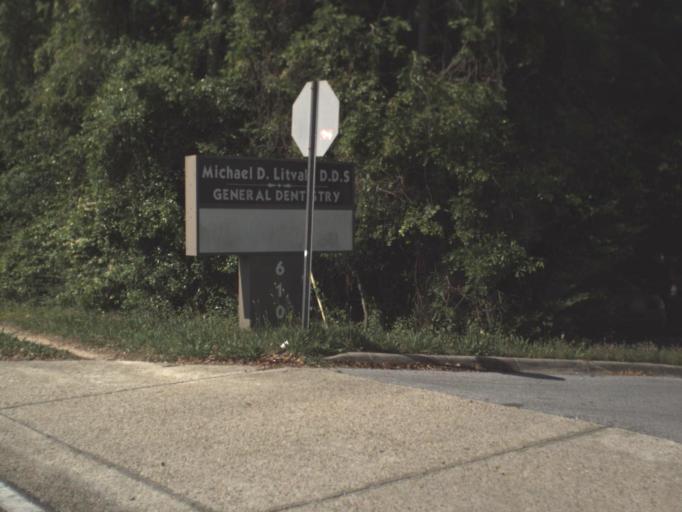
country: US
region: Florida
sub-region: Escambia County
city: Brent
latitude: 30.4846
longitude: -87.2228
